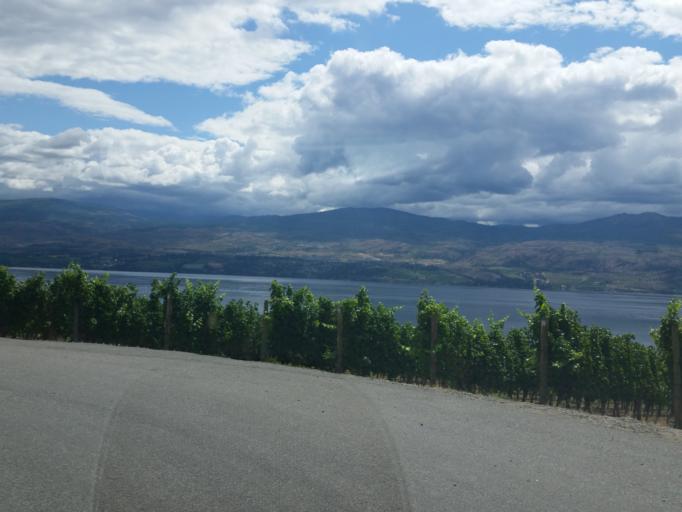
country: CA
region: British Columbia
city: West Kelowna
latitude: 49.8412
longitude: -119.5700
